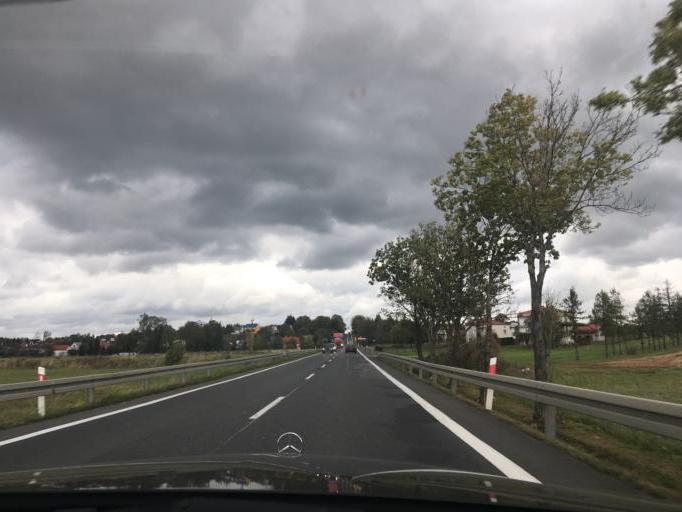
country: PL
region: Subcarpathian Voivodeship
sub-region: Powiat krosnienski
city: Miejsce Piastowe
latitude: 49.6430
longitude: 21.8040
